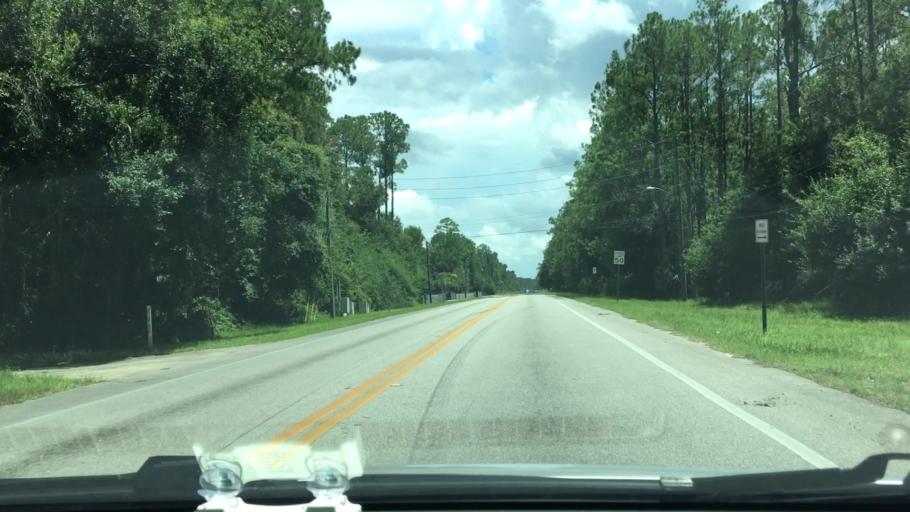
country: US
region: Florida
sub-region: Volusia County
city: Samsula-Spruce Creek
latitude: 29.0433
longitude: -81.0675
